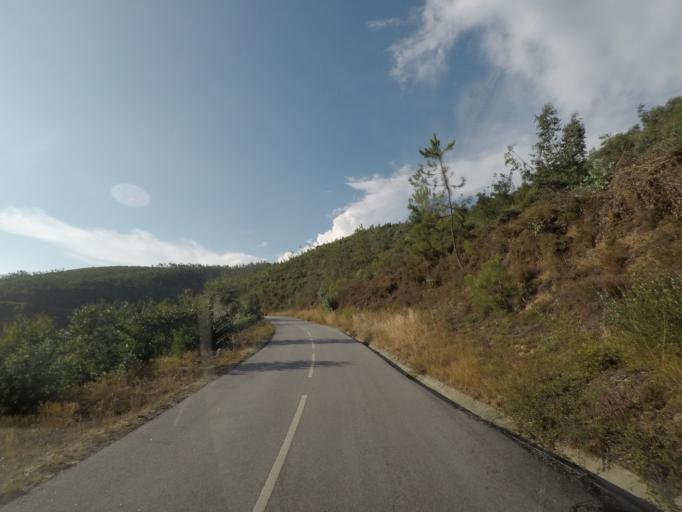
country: PT
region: Vila Real
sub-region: Mesao Frio
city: Mesao Frio
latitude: 41.1629
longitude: -7.9067
